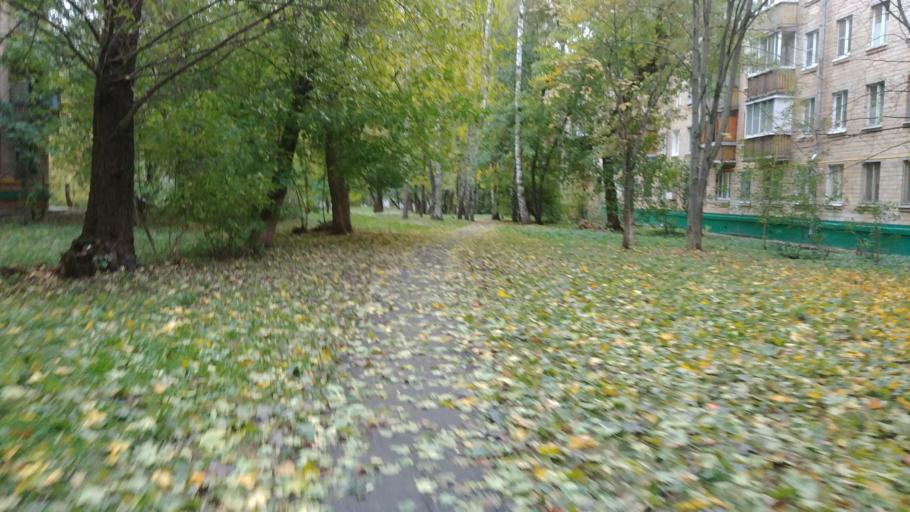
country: RU
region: Moscow
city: Golovinskiy
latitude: 55.8447
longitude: 37.4944
